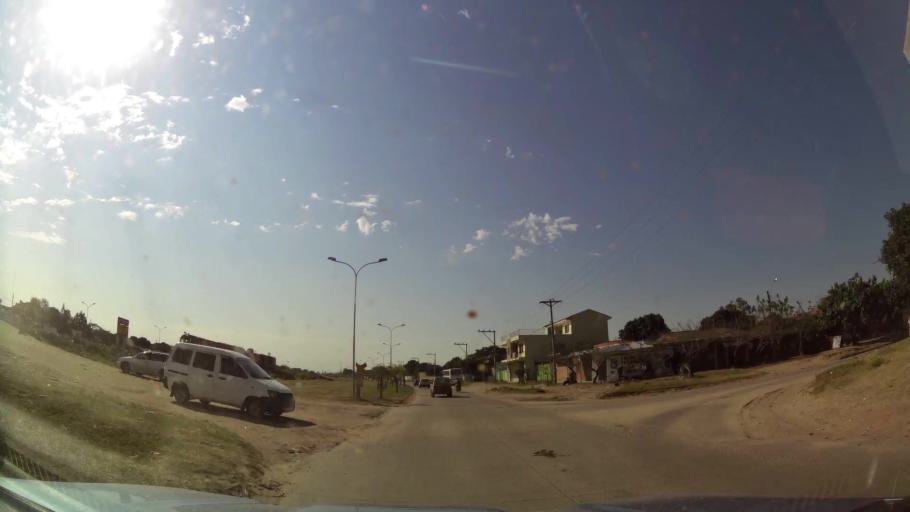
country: BO
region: Santa Cruz
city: Santa Cruz de la Sierra
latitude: -17.8072
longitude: -63.1408
